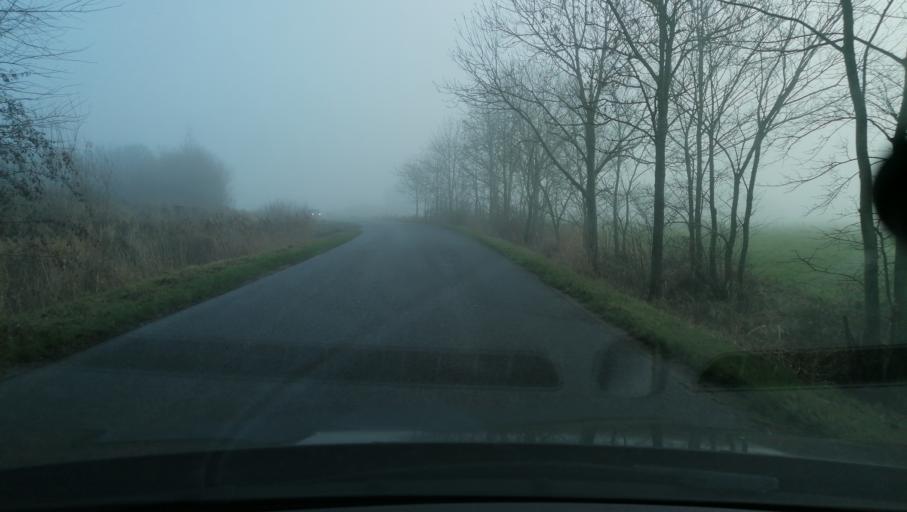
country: DE
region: Schleswig-Holstein
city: Epenwohrden
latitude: 54.1000
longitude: 9.0523
